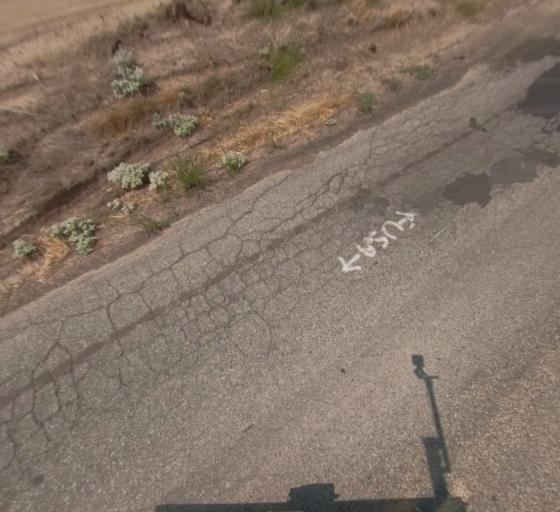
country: US
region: California
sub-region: Madera County
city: Fairmead
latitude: 37.1267
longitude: -120.1202
